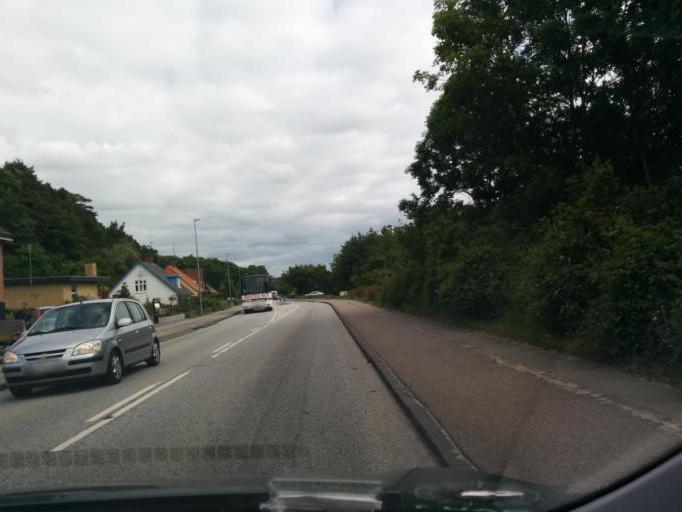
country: DK
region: Central Jutland
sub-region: Syddjurs Kommune
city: Ryomgard
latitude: 56.3805
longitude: 10.5076
